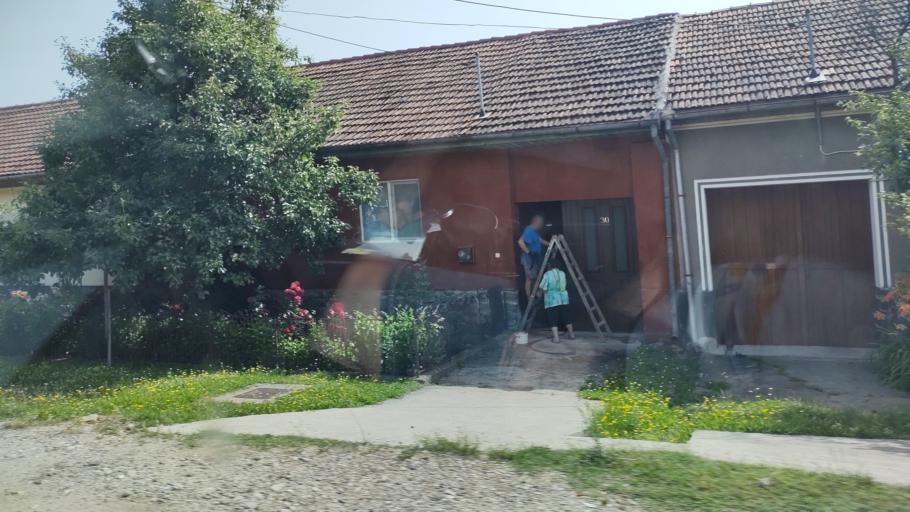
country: RO
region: Mehedinti
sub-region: Comuna Eselnita
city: Eselnita
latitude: 44.7085
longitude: 22.3597
